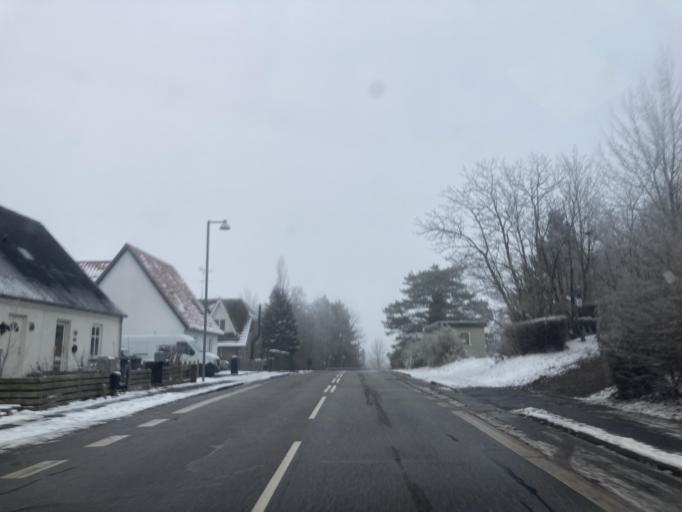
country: DK
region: Zealand
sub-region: Soro Kommune
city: Stenlille
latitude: 55.5433
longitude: 11.5985
